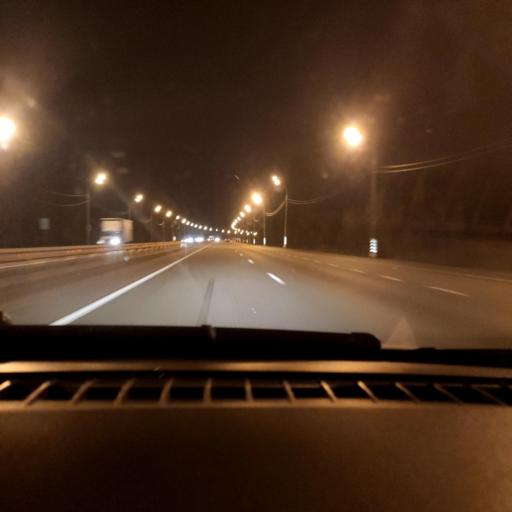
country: RU
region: Lipetsk
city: Khlevnoye
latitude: 52.2601
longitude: 39.0636
